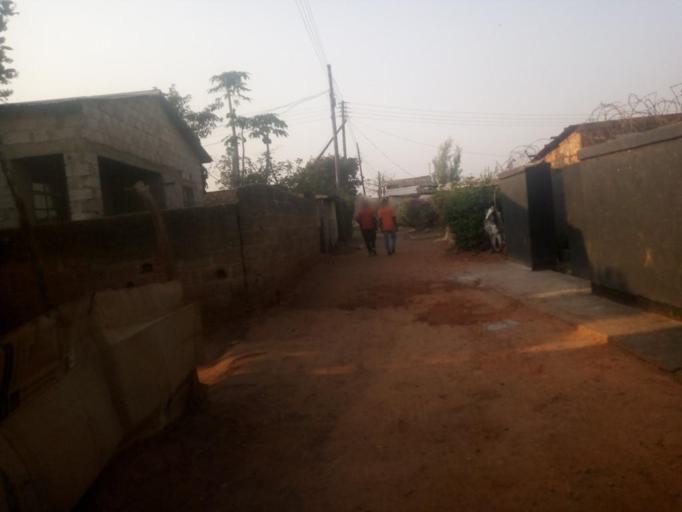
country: ZM
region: Lusaka
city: Lusaka
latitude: -15.4086
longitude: 28.3658
